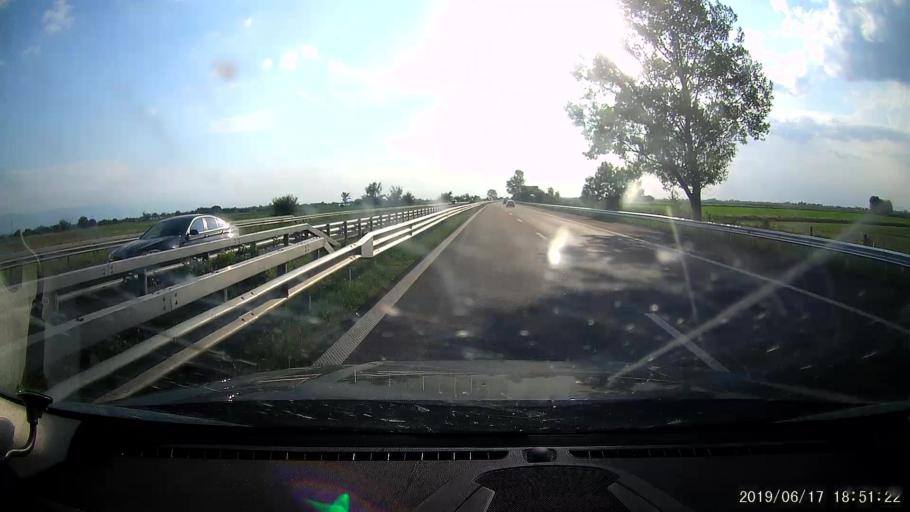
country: BG
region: Plovdiv
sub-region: Obshtina Rakovski
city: Rakovski
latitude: 42.2136
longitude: 24.9738
